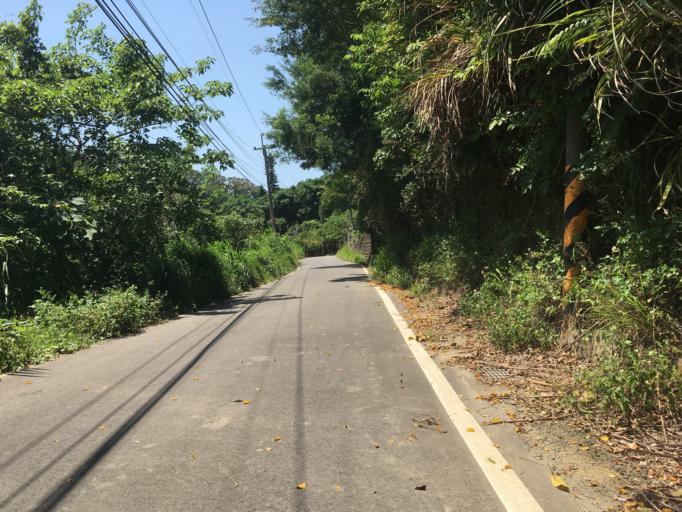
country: TW
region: Taiwan
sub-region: Hsinchu
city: Hsinchu
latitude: 24.7301
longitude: 120.9829
